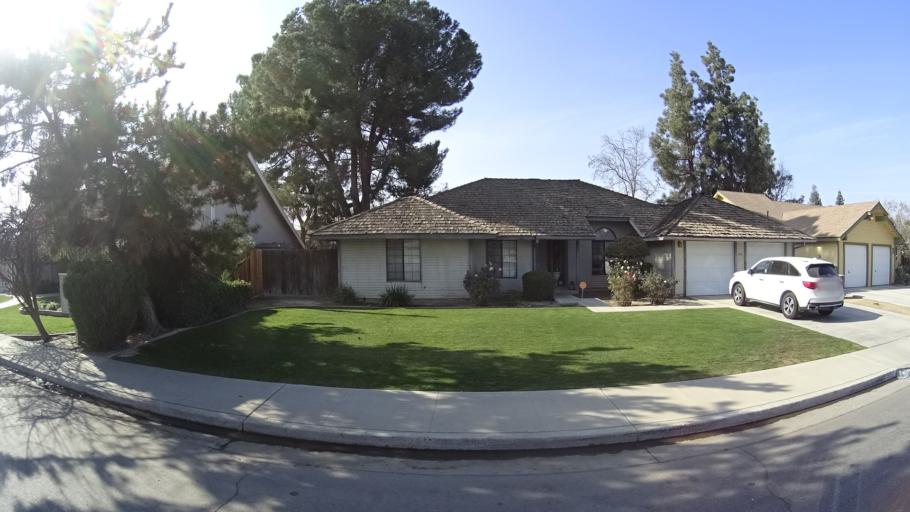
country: US
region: California
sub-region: Kern County
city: Bakersfield
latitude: 35.3225
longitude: -119.0515
